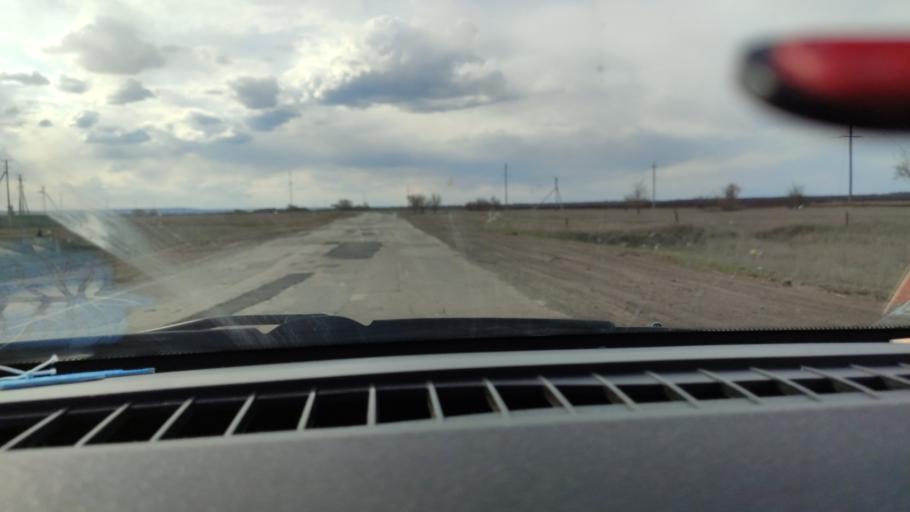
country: RU
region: Saratov
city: Rovnoye
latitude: 51.0635
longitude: 46.0152
